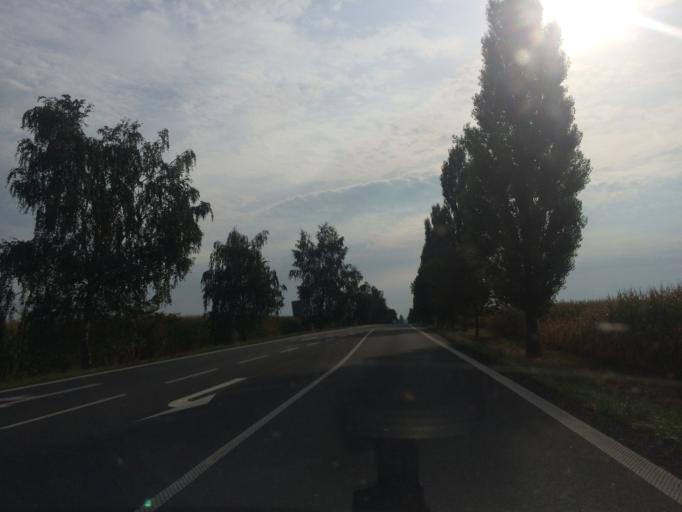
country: CZ
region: Central Bohemia
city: Poricany
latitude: 50.0510
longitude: 14.9365
